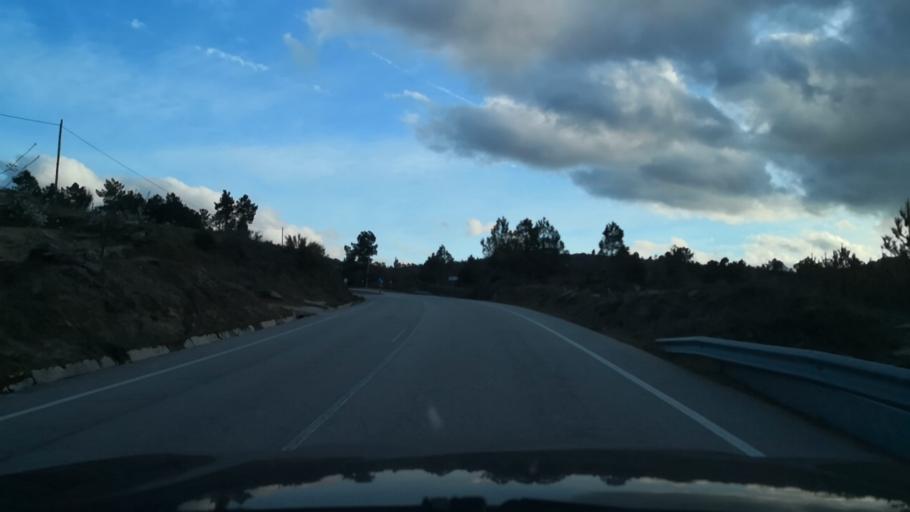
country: PT
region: Braganca
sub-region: Carrazeda de Ansiaes
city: Carrazeda de Anciaes
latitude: 41.2647
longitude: -7.3249
